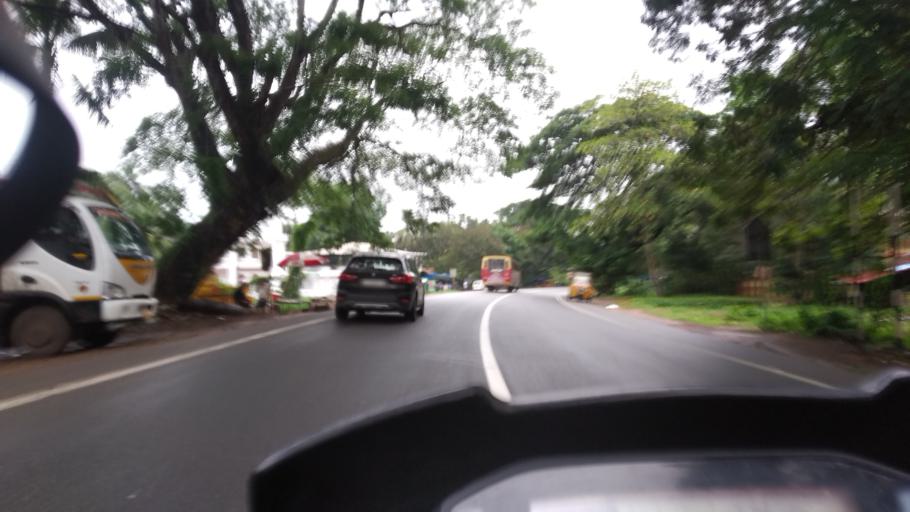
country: IN
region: Kerala
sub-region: Alappuzha
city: Mavelikara
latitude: 9.2843
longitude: 76.4403
